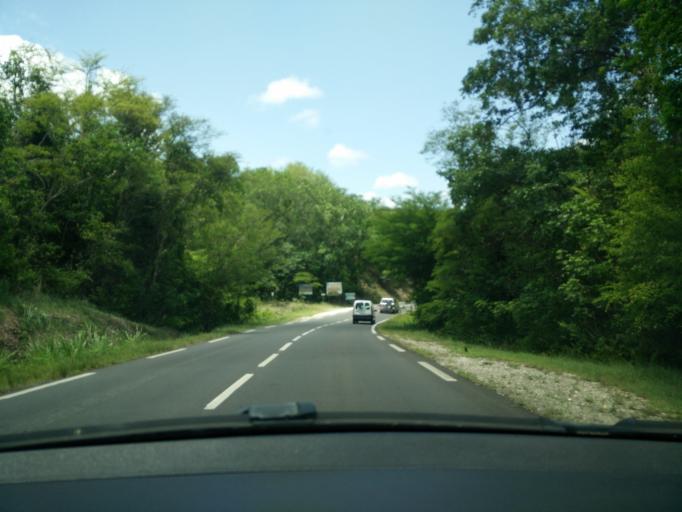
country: GP
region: Guadeloupe
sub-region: Guadeloupe
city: Sainte-Rose
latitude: 16.3500
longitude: -61.7665
